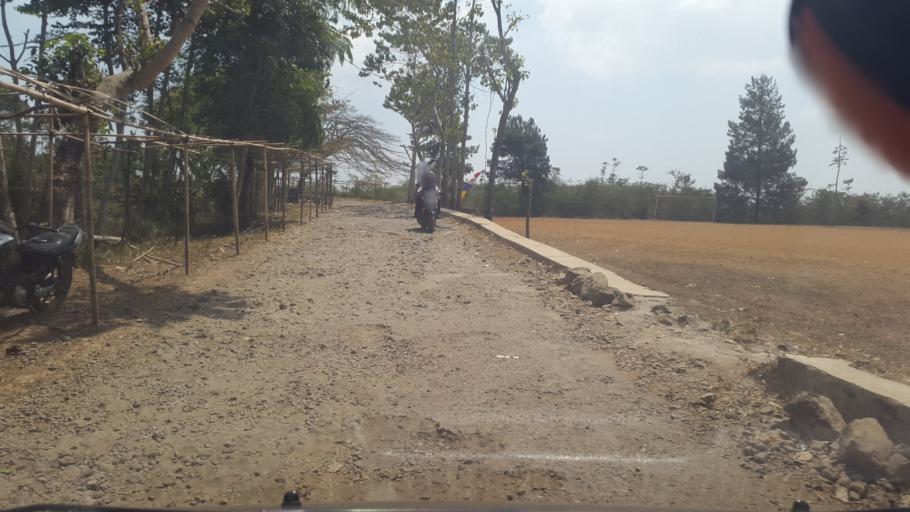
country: ID
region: West Java
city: Cigenca
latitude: -7.0940
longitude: 106.6737
